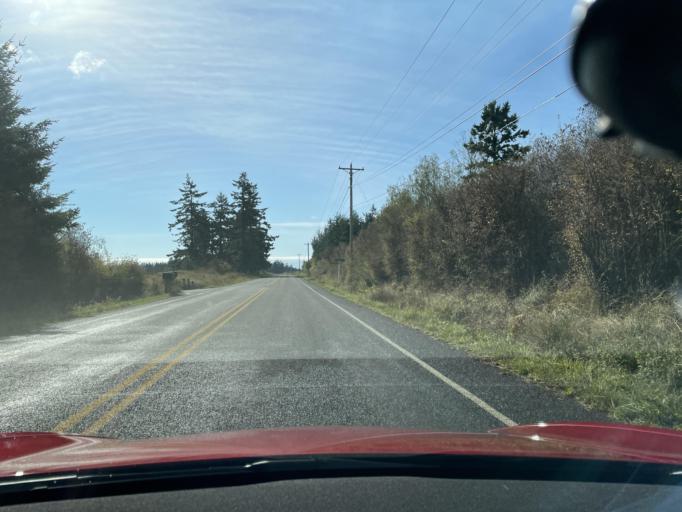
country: US
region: Washington
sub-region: San Juan County
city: Friday Harbor
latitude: 48.4798
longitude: -123.0322
